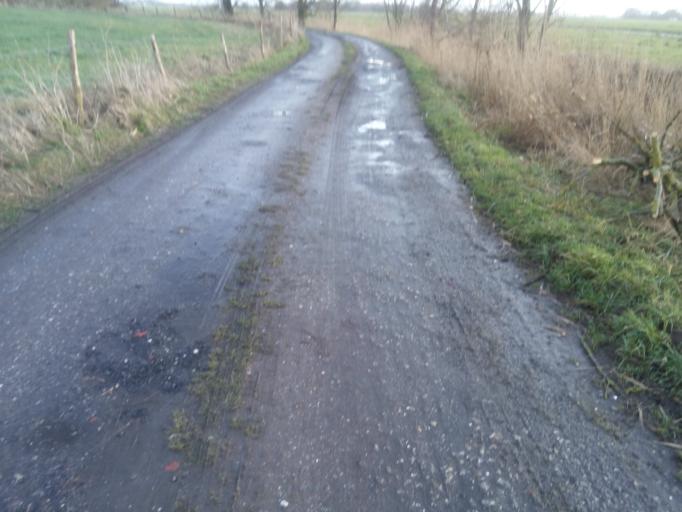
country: NL
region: Groningen
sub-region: Gemeente Zuidhorn
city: Aduard
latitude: 53.2783
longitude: 6.4453
